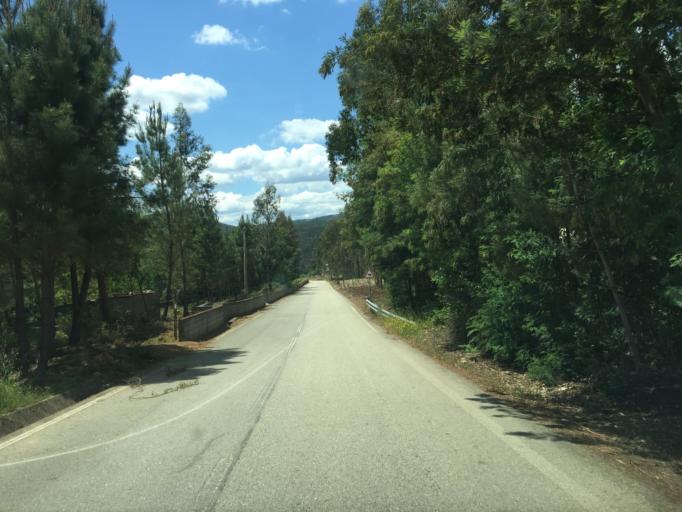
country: PT
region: Coimbra
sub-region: Pampilhosa da Serra
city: Pampilhosa da Serra
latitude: 40.0752
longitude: -7.7963
